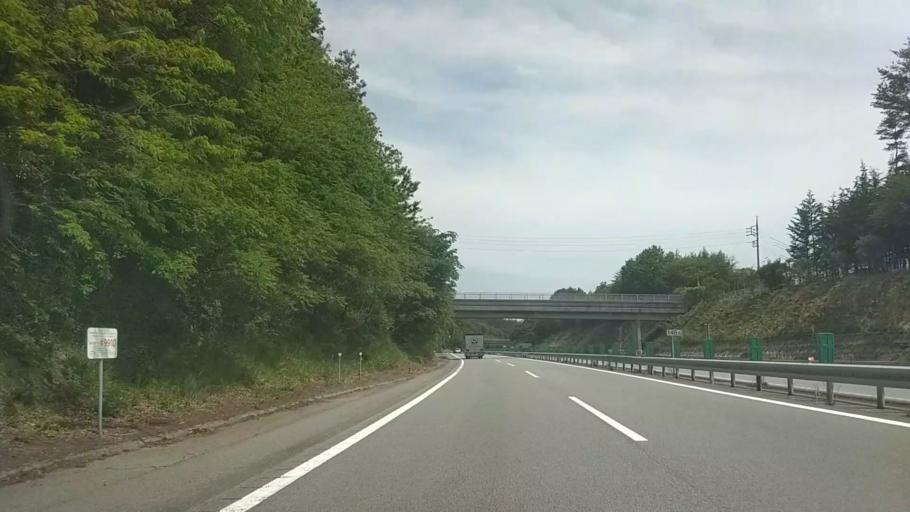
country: JP
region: Yamanashi
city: Nirasaki
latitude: 35.8632
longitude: 138.3270
